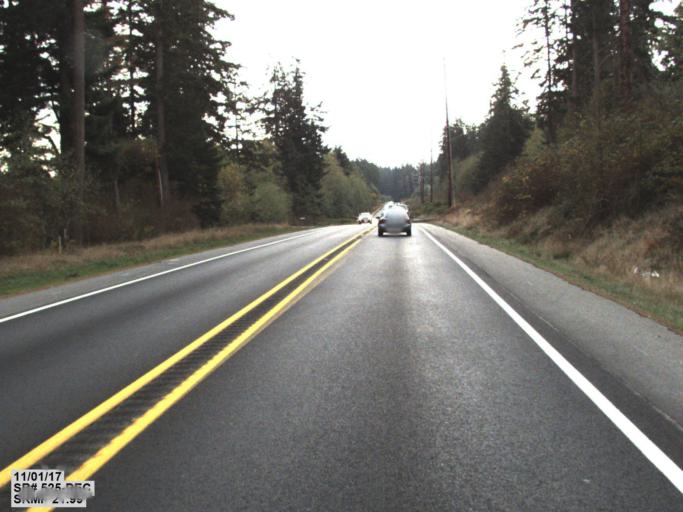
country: US
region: Washington
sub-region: Island County
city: Freeland
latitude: 48.0546
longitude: -122.5669
